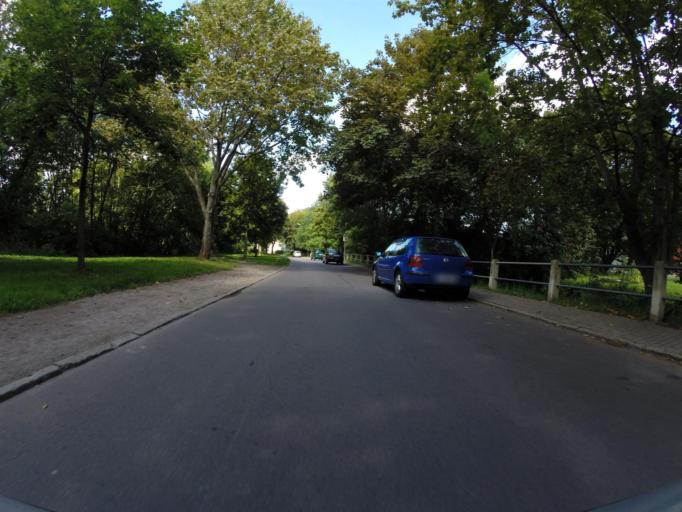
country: DE
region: Thuringia
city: Erfurt
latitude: 50.9935
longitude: 11.0215
